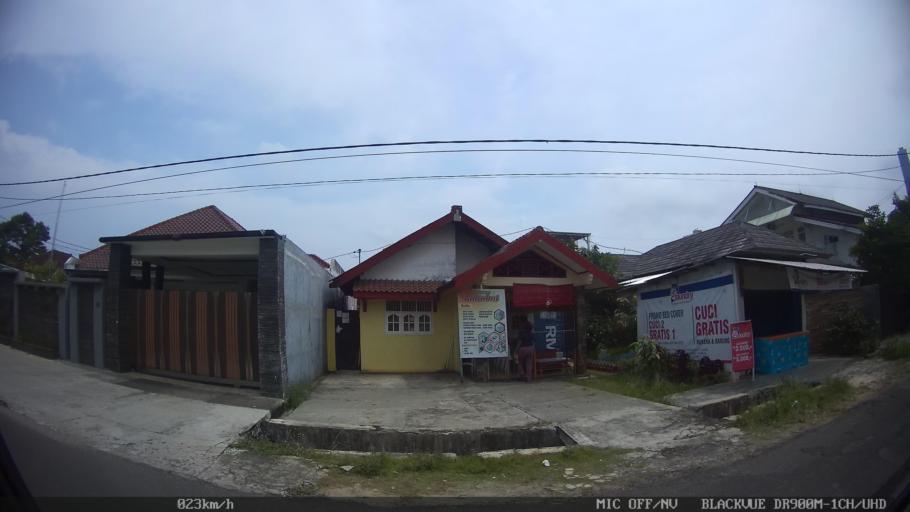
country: ID
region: Lampung
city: Bandarlampung
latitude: -5.4179
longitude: 105.2643
